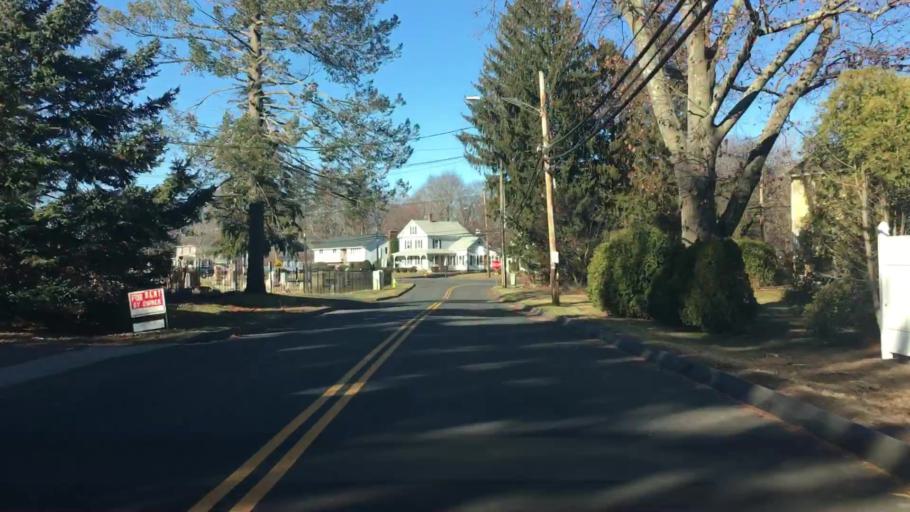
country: US
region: Connecticut
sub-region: Tolland County
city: Rockville
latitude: 41.8668
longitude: -72.4281
